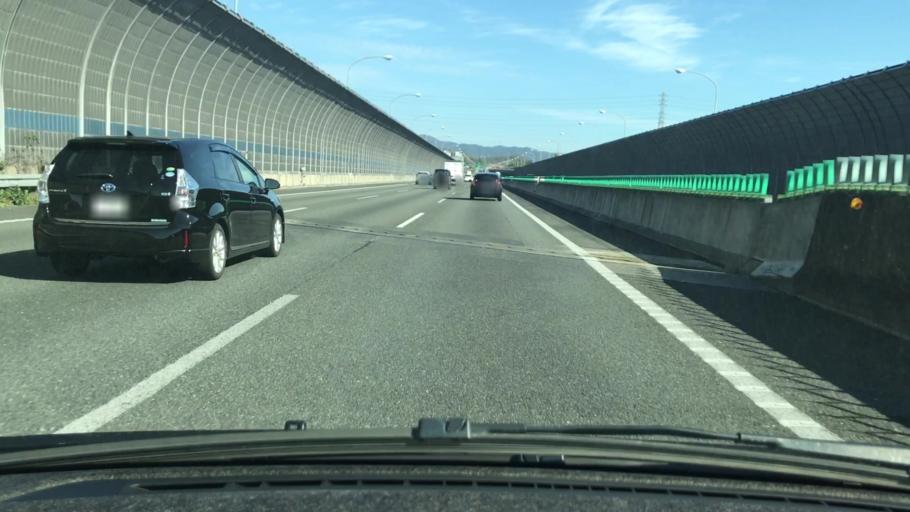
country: JP
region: Osaka
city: Ibaraki
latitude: 34.8382
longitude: 135.5673
